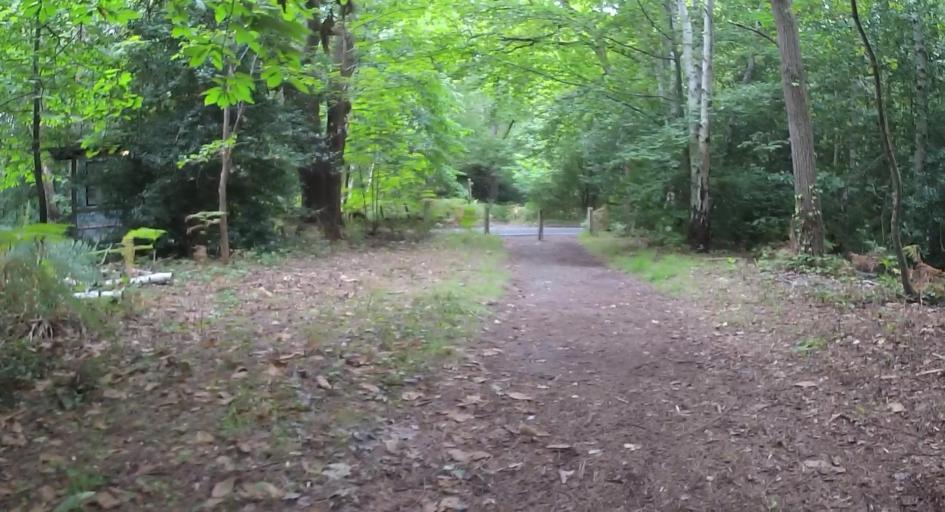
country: GB
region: England
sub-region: Surrey
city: West Byfleet
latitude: 51.3214
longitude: -0.5200
